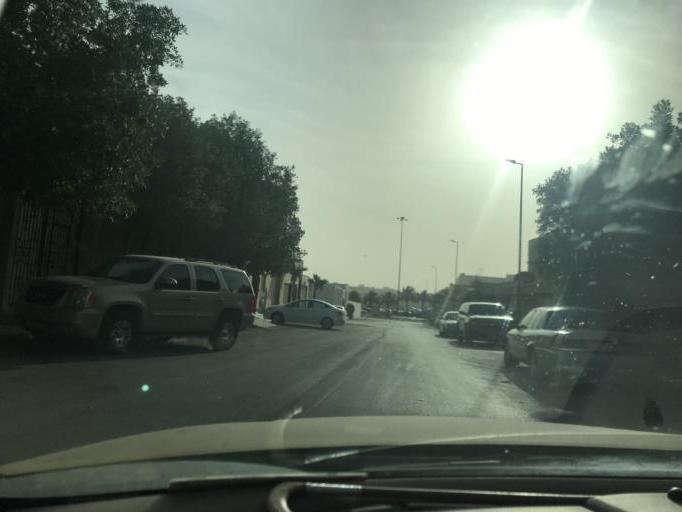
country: SA
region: Ar Riyad
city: Riyadh
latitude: 24.7377
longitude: 46.7520
